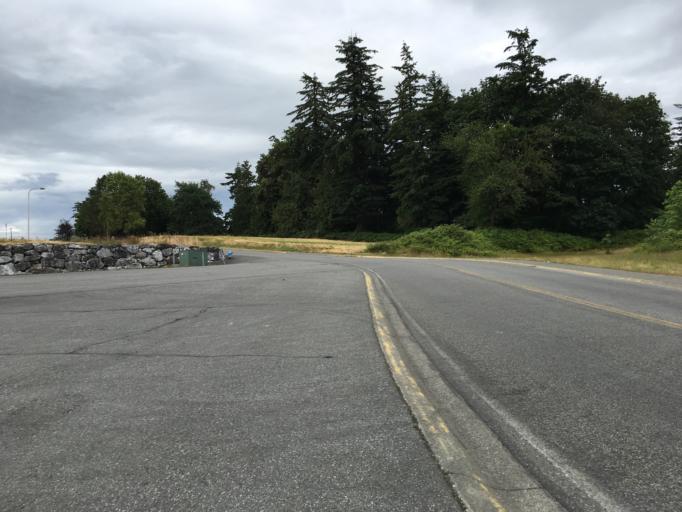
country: US
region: Washington
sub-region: Whatcom County
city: Lynden
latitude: 48.9368
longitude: -122.4817
